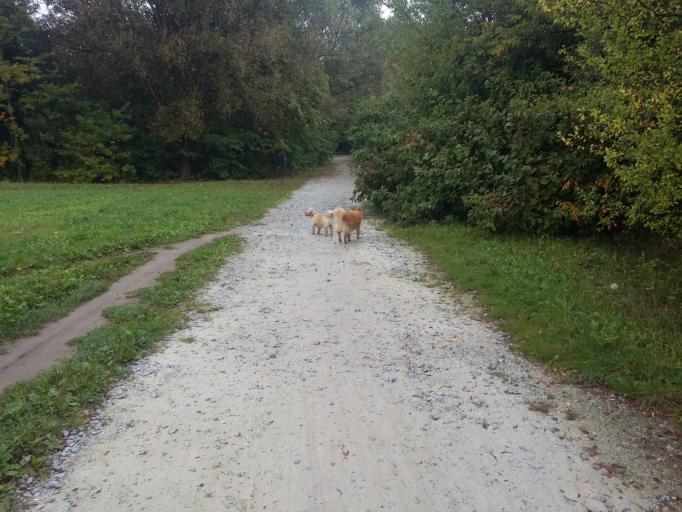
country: PL
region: Lodz Voivodeship
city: Lodz
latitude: 51.7536
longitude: 19.3974
